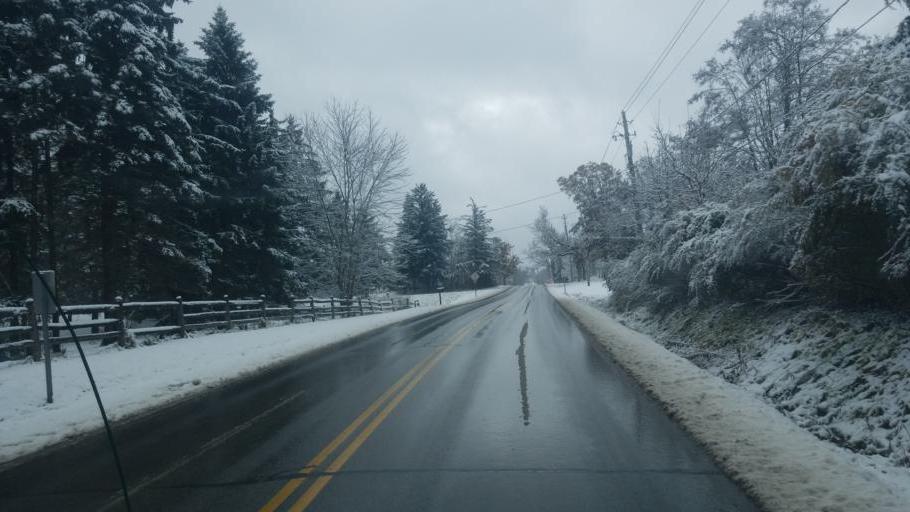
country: US
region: Ohio
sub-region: Geauga County
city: Middlefield
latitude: 41.4329
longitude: -81.0525
